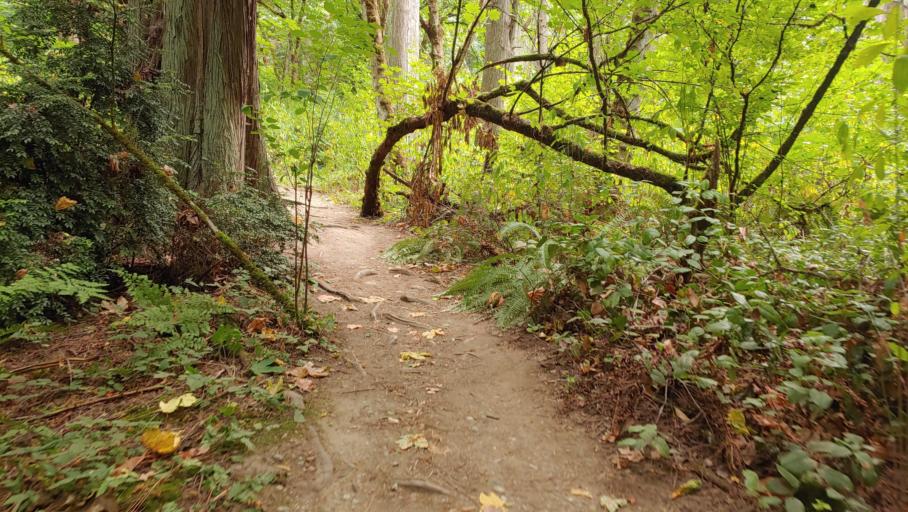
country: US
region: Washington
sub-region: King County
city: Mercer Island
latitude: 47.5605
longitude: -122.2524
